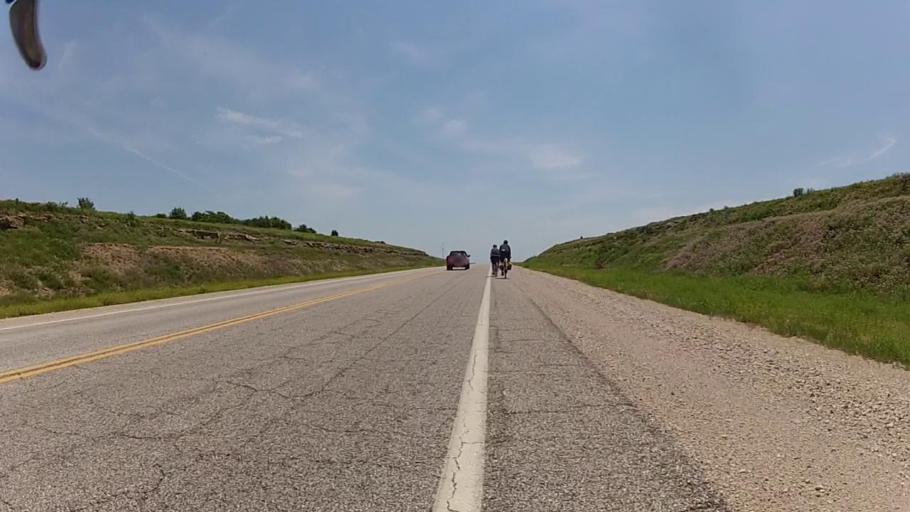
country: US
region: Kansas
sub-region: Chautauqua County
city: Sedan
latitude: 37.1140
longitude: -96.4711
